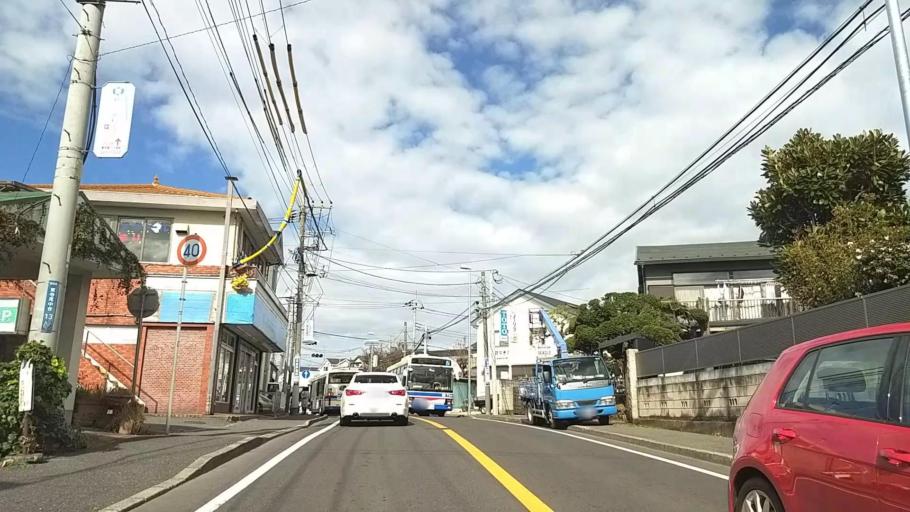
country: JP
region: Kanagawa
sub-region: Kawasaki-shi
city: Kawasaki
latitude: 35.5102
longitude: 139.6643
